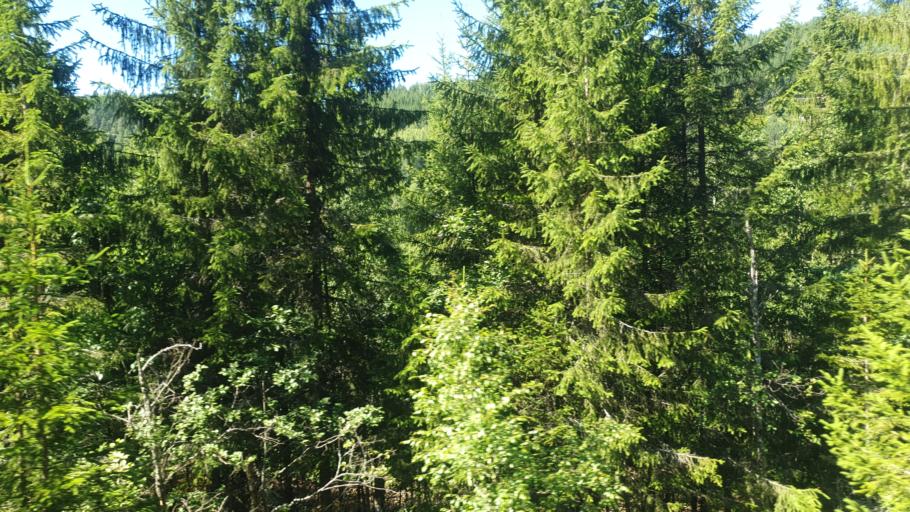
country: NO
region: Sor-Trondelag
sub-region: Meldal
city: Meldal
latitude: 63.1394
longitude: 9.7119
